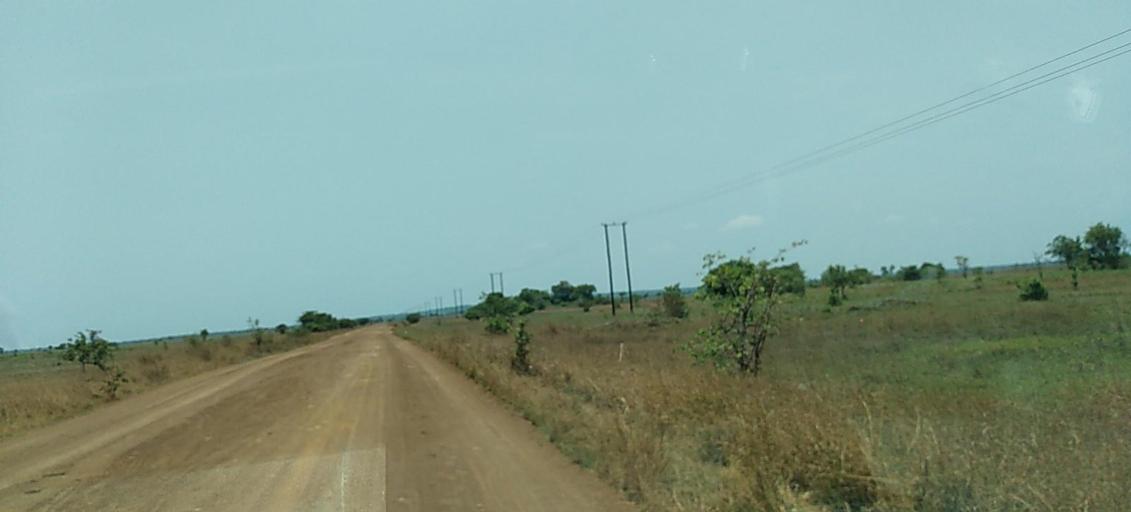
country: ZM
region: Copperbelt
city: Mpongwe
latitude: -13.6681
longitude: 27.8535
